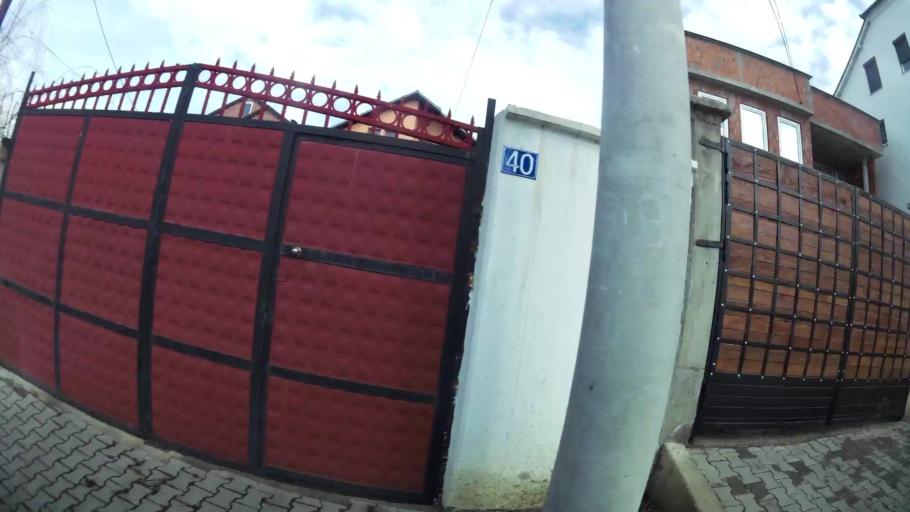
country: XK
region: Pristina
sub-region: Komuna e Prishtines
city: Pristina
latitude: 42.6776
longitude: 21.1549
